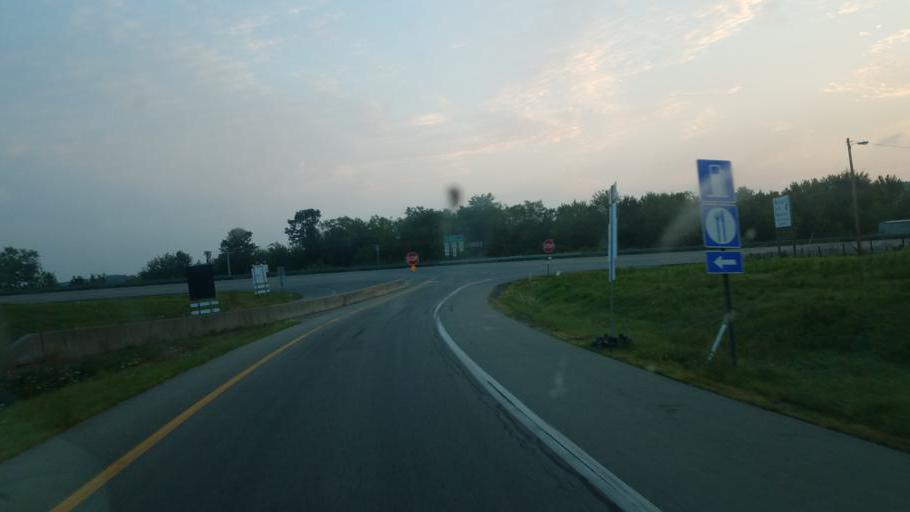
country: US
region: Pennsylvania
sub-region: Crawford County
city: Meadville
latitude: 41.5378
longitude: -80.1811
